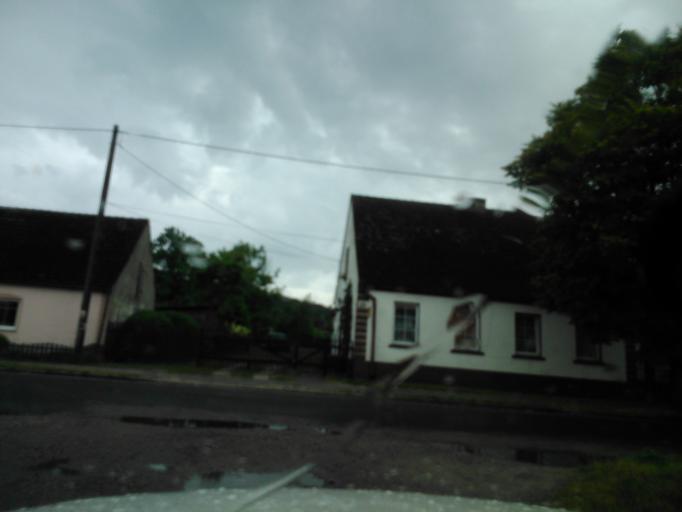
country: PL
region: Pomeranian Voivodeship
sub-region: Powiat slupski
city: Smoldzino
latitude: 54.6647
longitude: 17.2148
